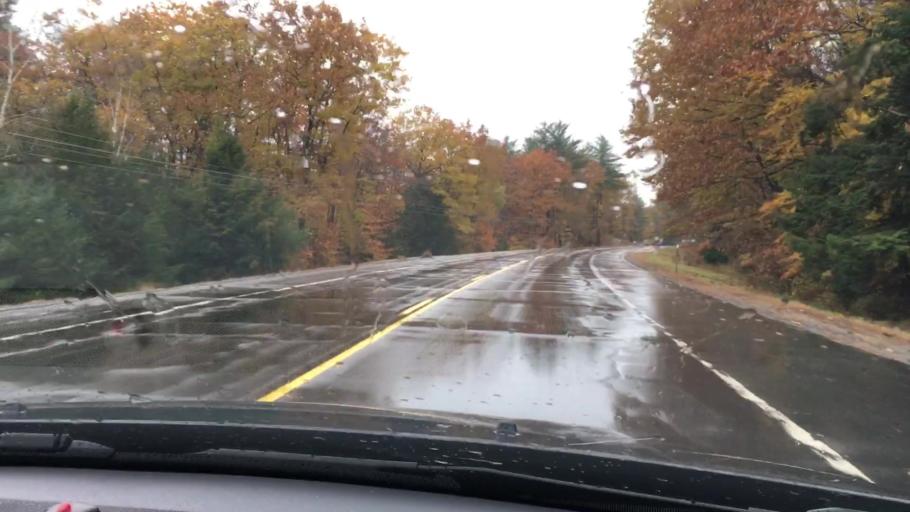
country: US
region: New Hampshire
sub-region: Grafton County
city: Ashland
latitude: 43.7131
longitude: -71.6252
